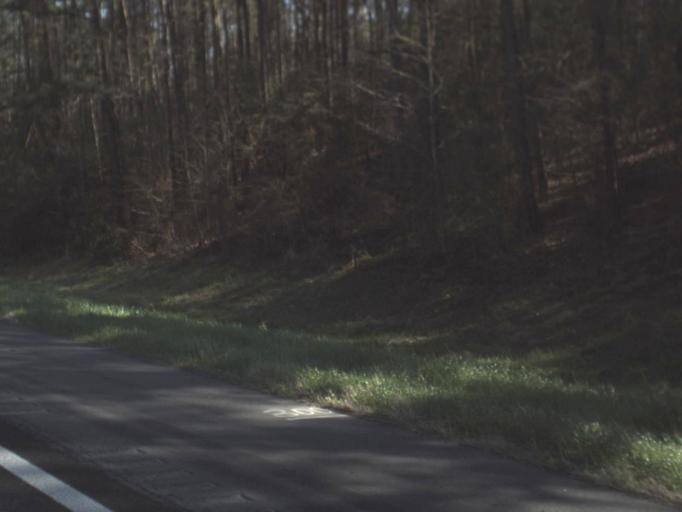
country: US
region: Florida
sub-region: Gadsden County
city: Chattahoochee
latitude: 30.6200
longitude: -84.8364
